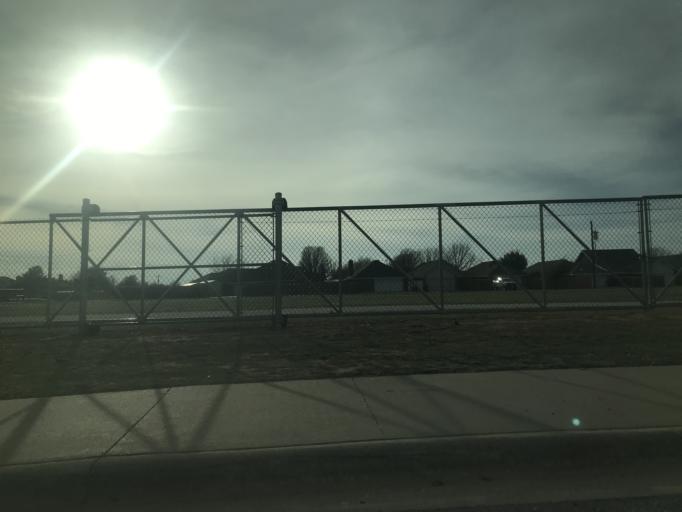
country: US
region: Texas
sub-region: Taylor County
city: Abilene
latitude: 32.3984
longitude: -99.7720
